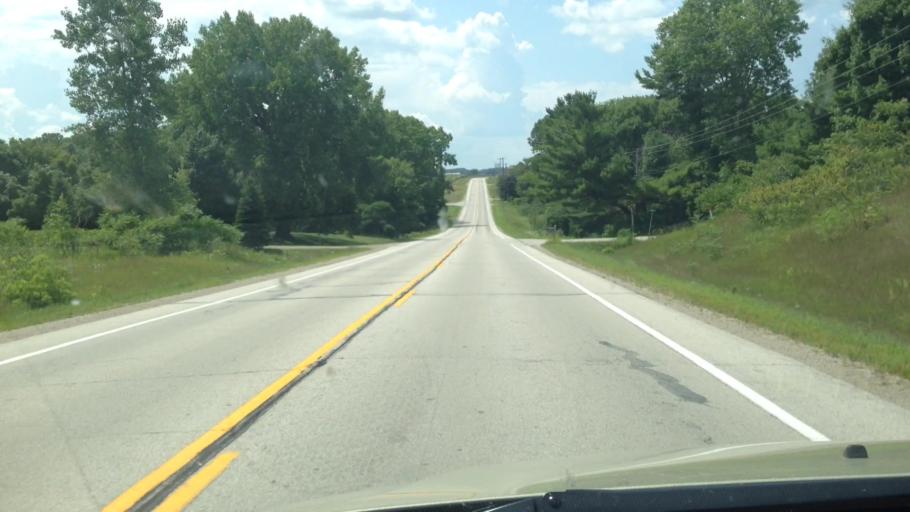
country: US
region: Wisconsin
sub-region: Brown County
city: Suamico
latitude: 44.6474
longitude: -88.1409
